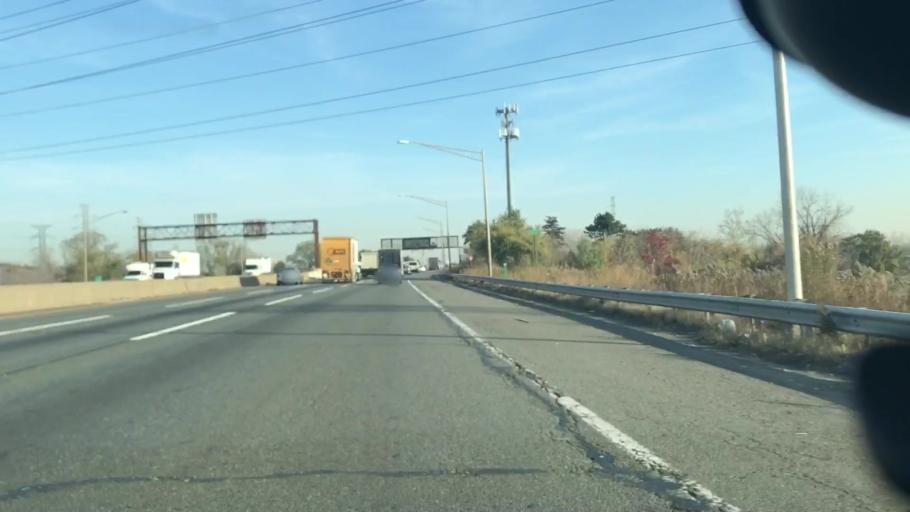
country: US
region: New Jersey
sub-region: Hudson County
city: Kearny
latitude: 40.7574
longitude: -74.1167
